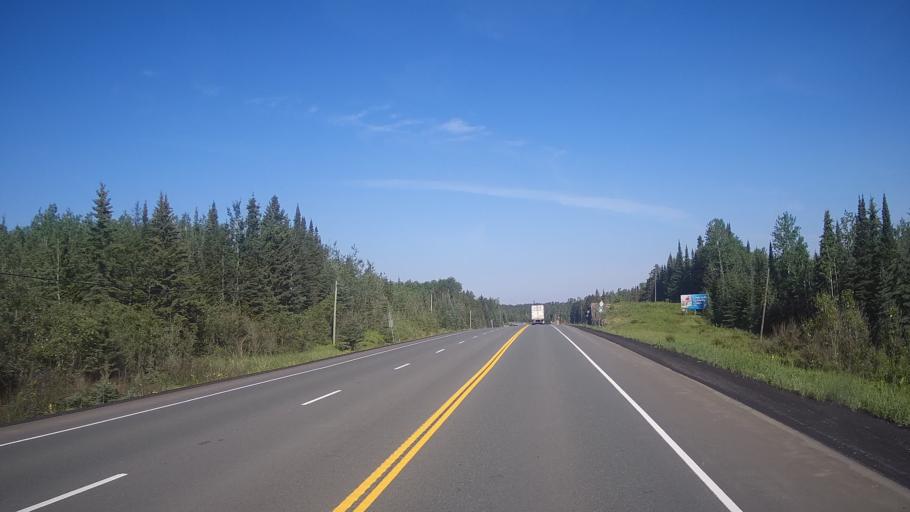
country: CA
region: Ontario
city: Dryden
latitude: 49.6449
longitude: -92.4477
